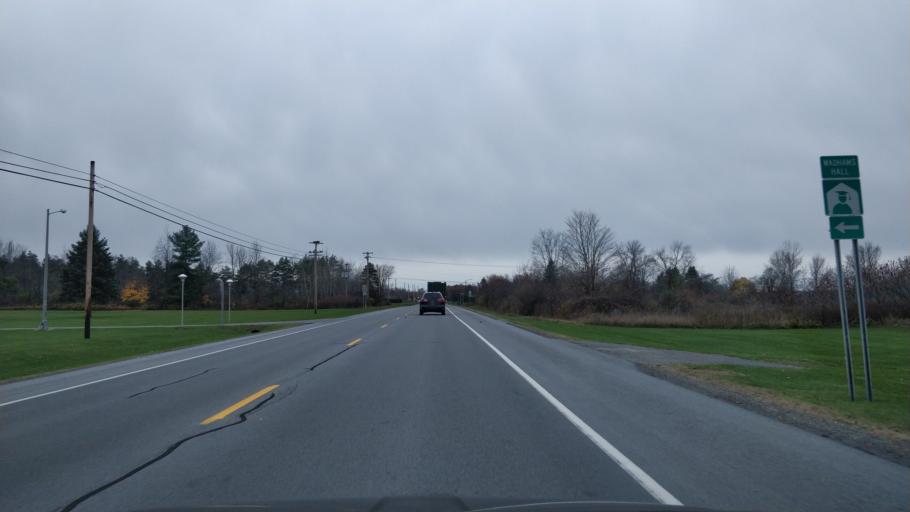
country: CA
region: Ontario
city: Prescott
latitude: 44.6674
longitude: -75.5358
